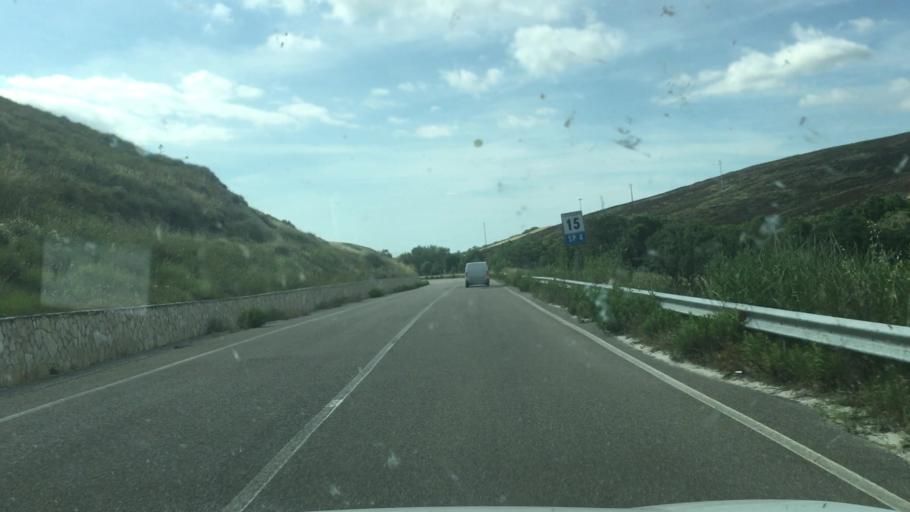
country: IT
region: Basilicate
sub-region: Provincia di Matera
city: Salandra
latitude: 40.5322
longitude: 16.2876
